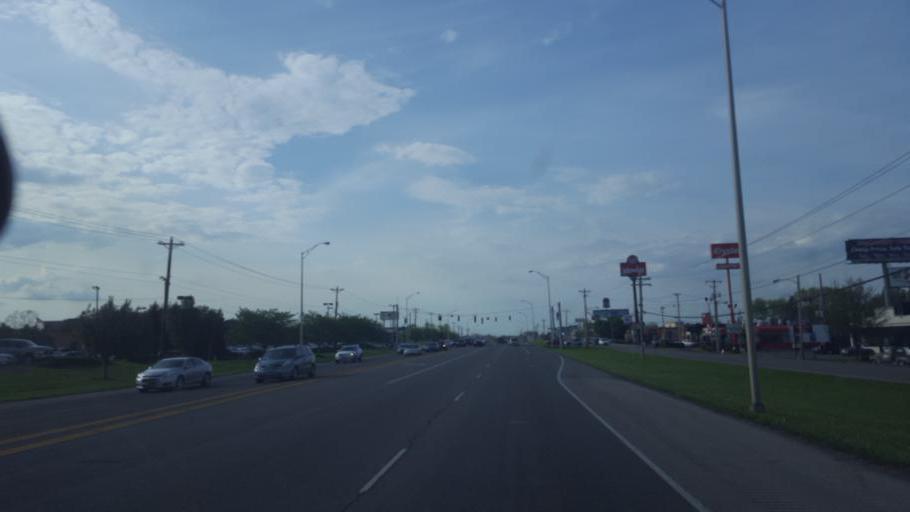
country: US
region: Kentucky
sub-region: Warren County
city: Bowling Green
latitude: 36.9475
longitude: -86.4238
